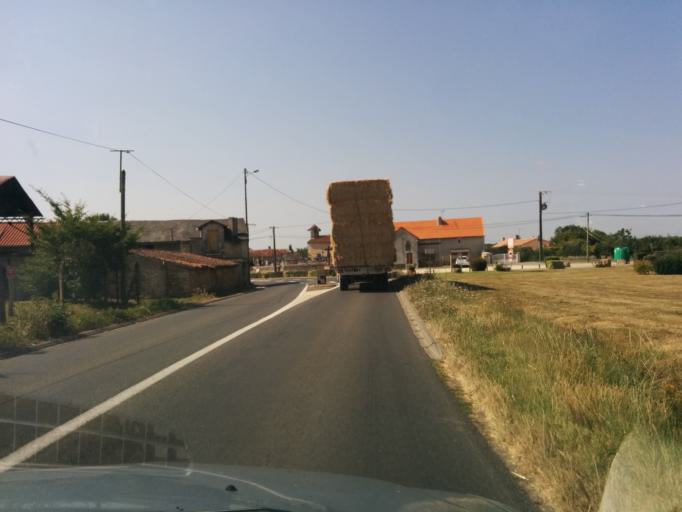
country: FR
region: Poitou-Charentes
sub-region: Departement de la Vienne
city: Mirebeau
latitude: 46.7446
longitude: 0.1783
